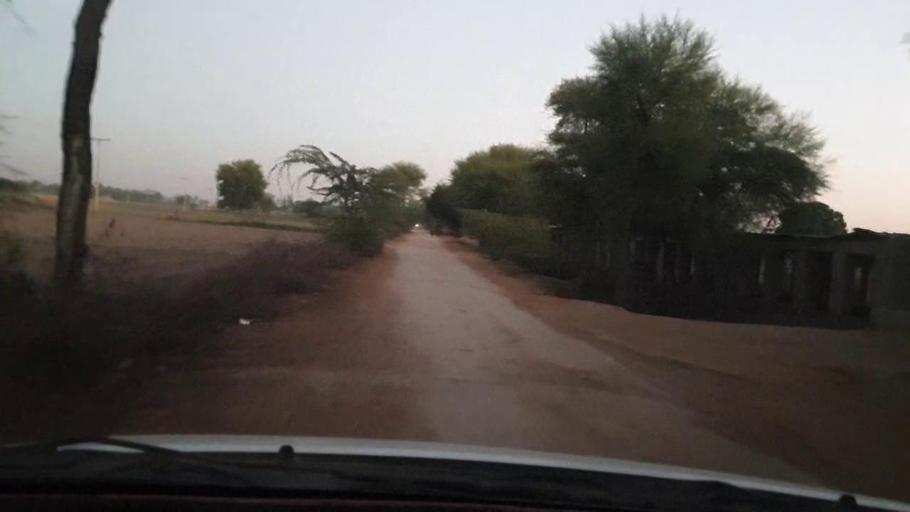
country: PK
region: Sindh
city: Khairpur Nathan Shah
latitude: 27.1351
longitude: 67.7207
